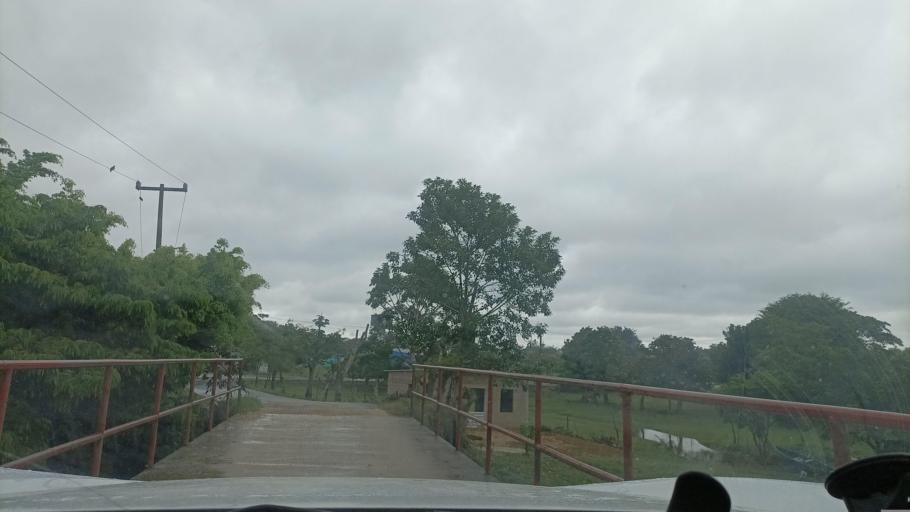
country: MX
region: Veracruz
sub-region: Moloacan
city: Cuichapa
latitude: 17.7601
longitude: -94.3936
